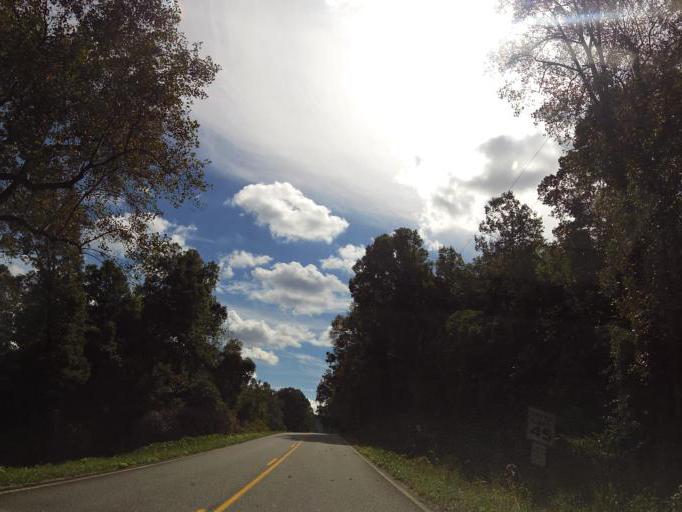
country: US
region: Georgia
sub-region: Pickens County
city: Nelson
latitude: 34.4669
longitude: -84.2595
